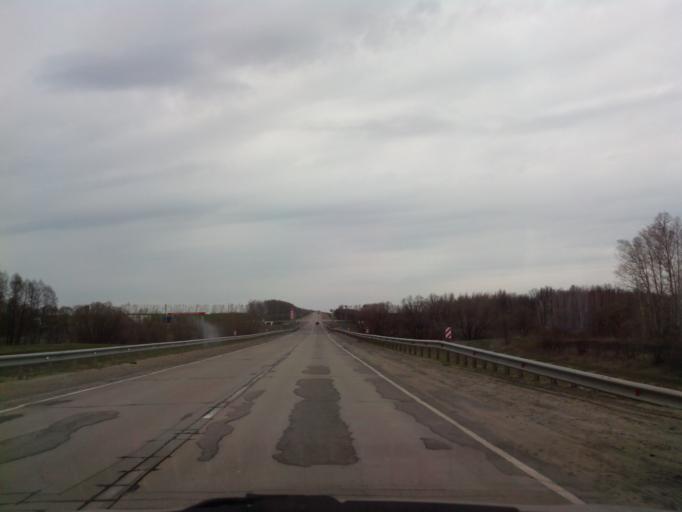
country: RU
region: Tambov
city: Znamenka
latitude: 52.4664
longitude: 41.3659
